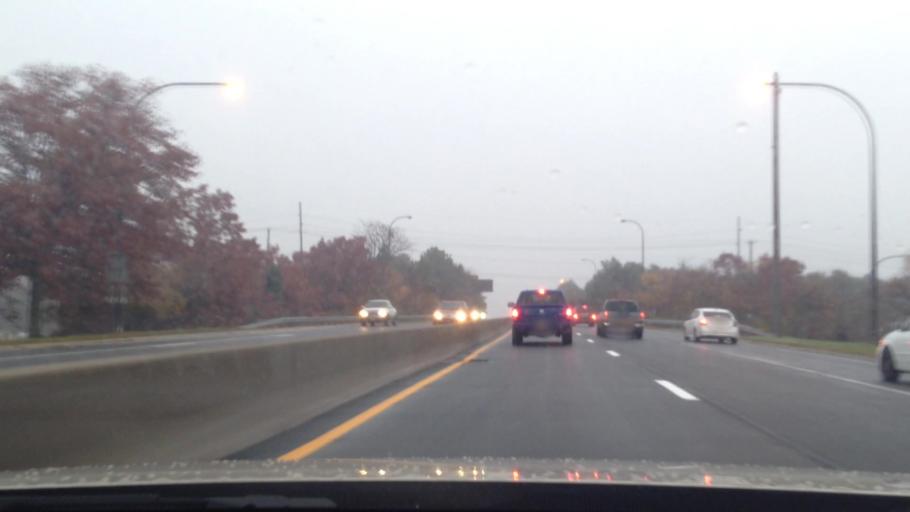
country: US
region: New York
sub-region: Suffolk County
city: Bay Wood
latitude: 40.7706
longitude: -73.2798
